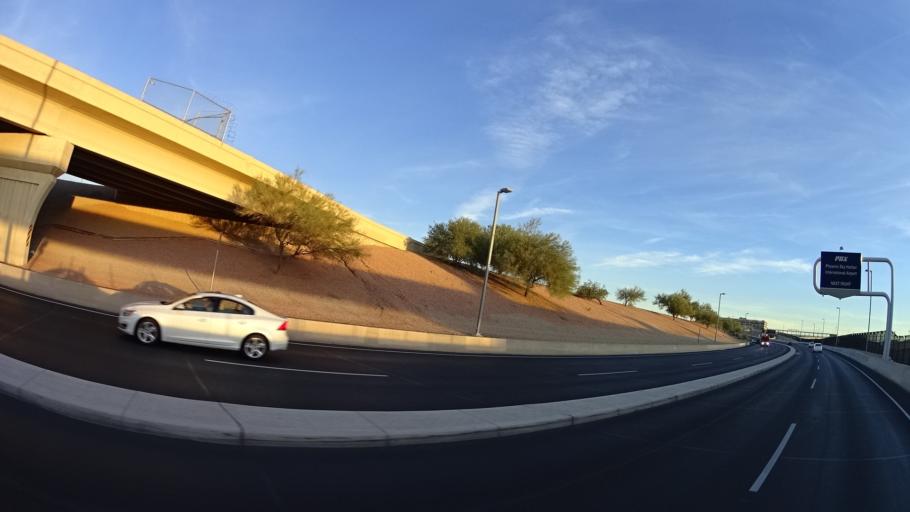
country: US
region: Arizona
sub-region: Maricopa County
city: Tempe Junction
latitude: 33.4412
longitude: -111.9877
